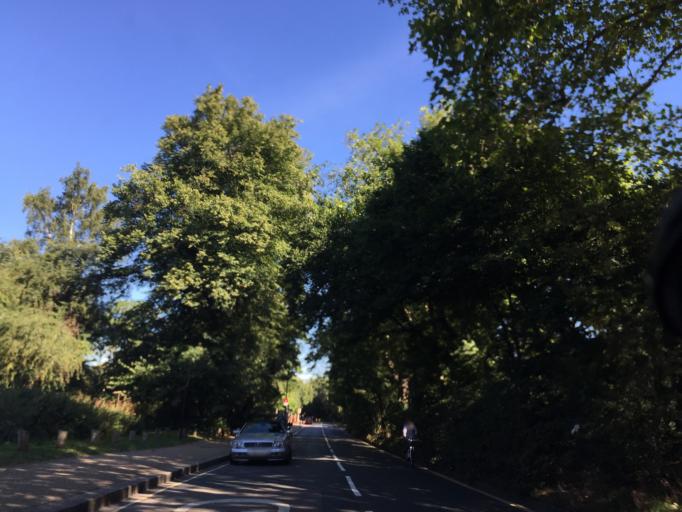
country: GB
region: England
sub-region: Greater London
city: Belsize Park
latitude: 51.5633
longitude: -0.1801
